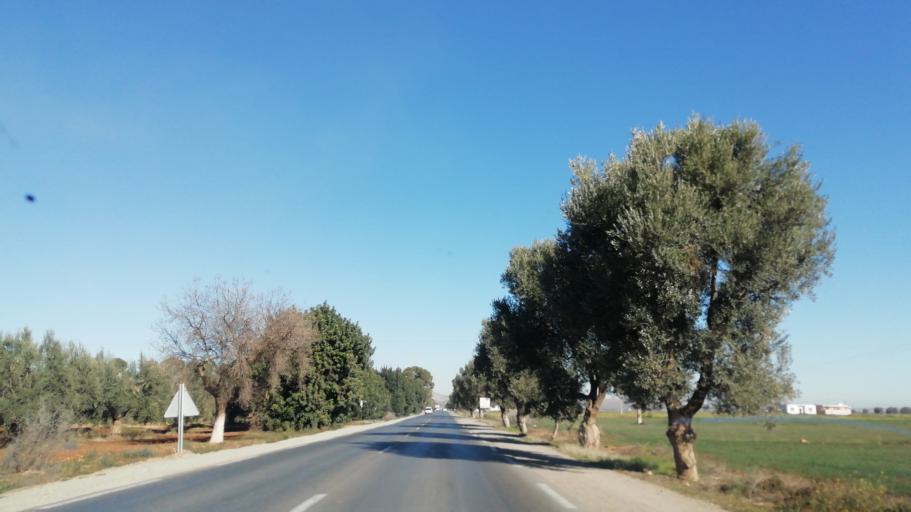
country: DZ
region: Mascara
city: Bou Hanifia el Hamamat
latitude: 35.1945
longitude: 0.1072
